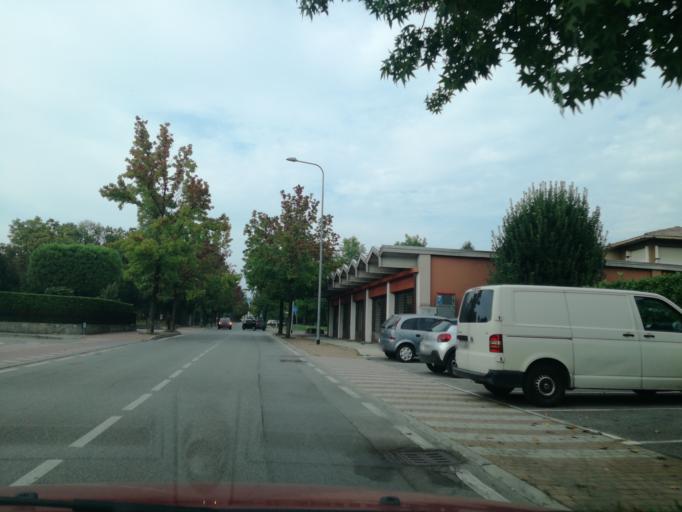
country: IT
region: Lombardy
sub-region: Provincia di Monza e Brianza
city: Carnate
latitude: 45.6422
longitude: 9.3792
